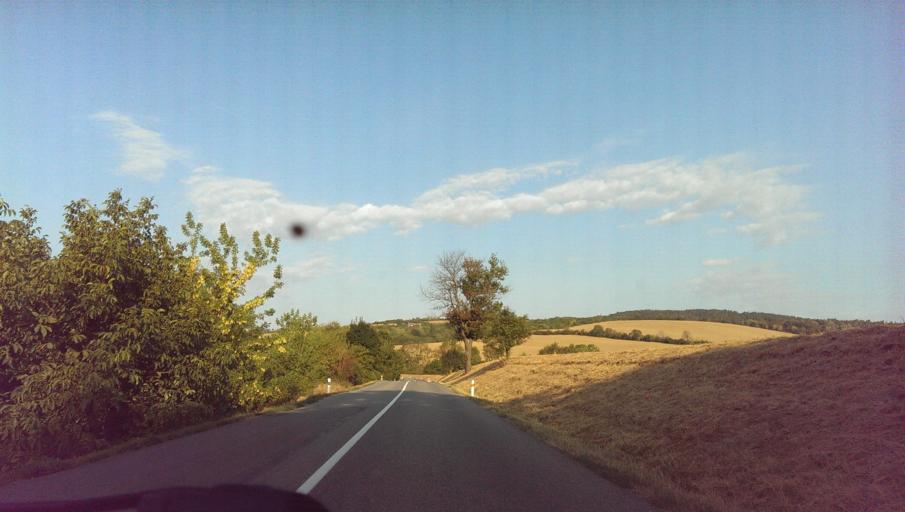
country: CZ
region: Zlin
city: Borsice
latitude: 49.0614
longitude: 17.3293
